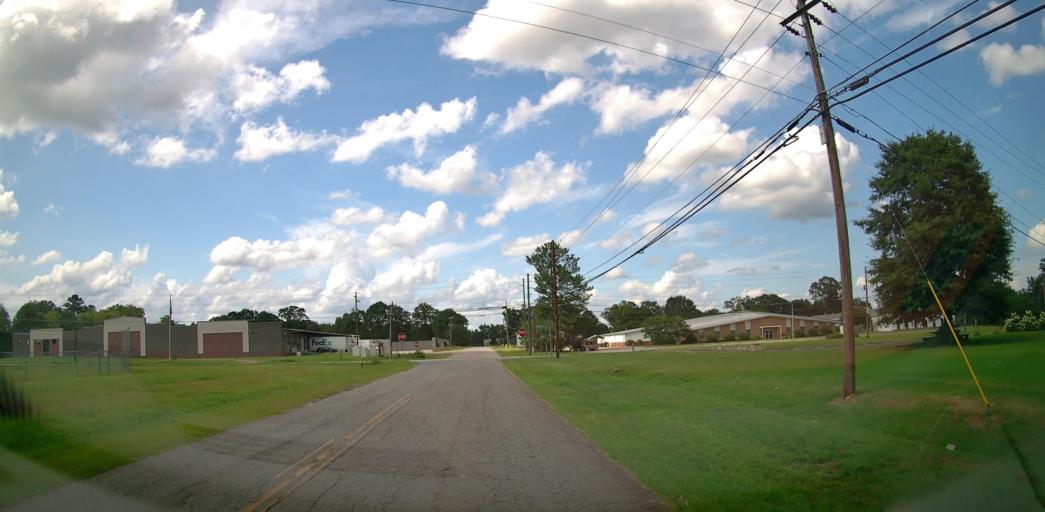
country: US
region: Georgia
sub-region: Houston County
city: Centerville
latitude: 32.7057
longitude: -83.6580
